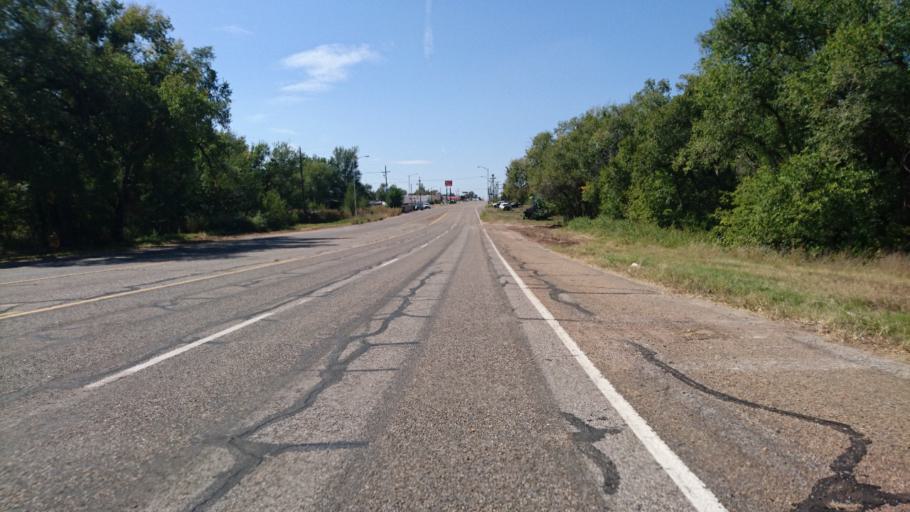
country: US
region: Texas
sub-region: Wheeler County
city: Shamrock
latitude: 35.2266
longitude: -100.2345
